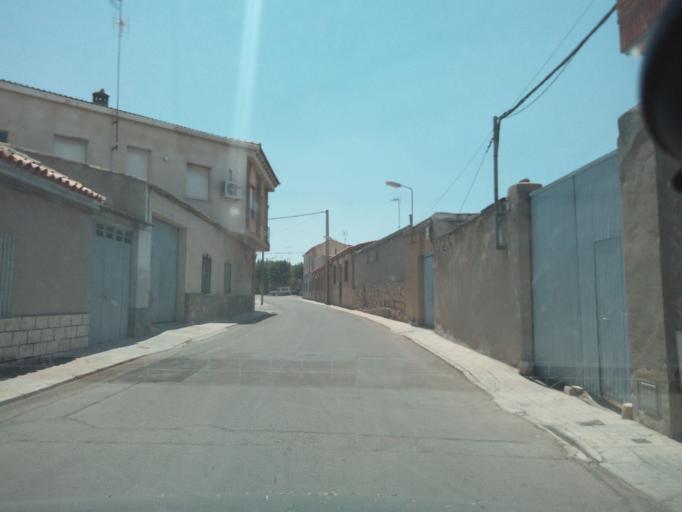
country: ES
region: Castille-La Mancha
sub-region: Province of Toledo
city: Villacanas
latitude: 39.6183
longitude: -3.3389
